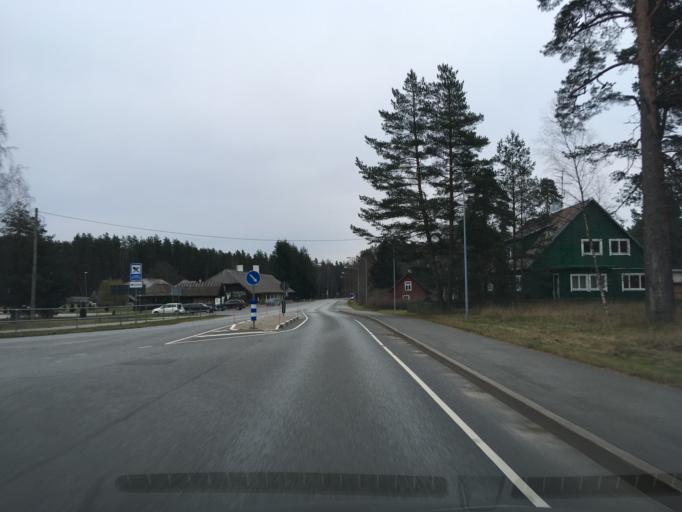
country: EE
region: Laeaene-Virumaa
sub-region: Kadrina vald
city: Kadrina
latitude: 59.4564
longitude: 26.0097
